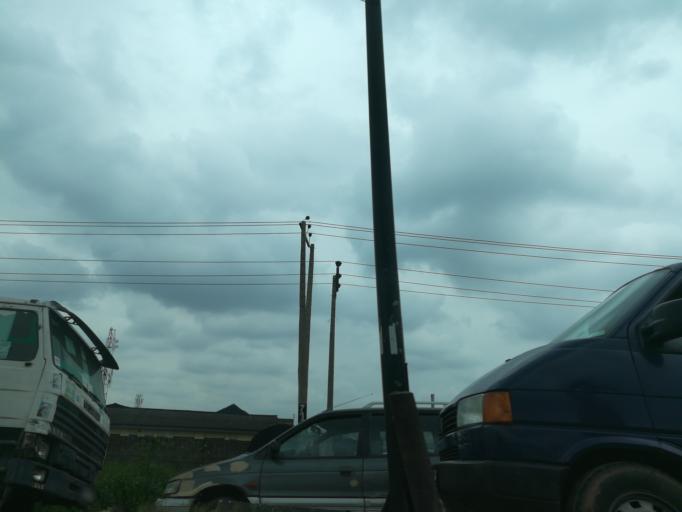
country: NG
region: Lagos
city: Ojota
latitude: 6.6090
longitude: 3.4093
